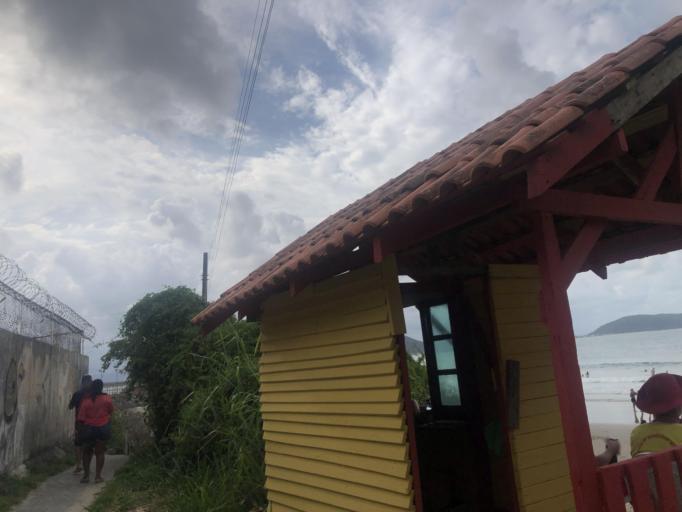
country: BR
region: Santa Catarina
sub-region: Sao Francisco Do Sul
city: Sao Francisco do Sul
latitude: -26.2189
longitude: -48.4980
